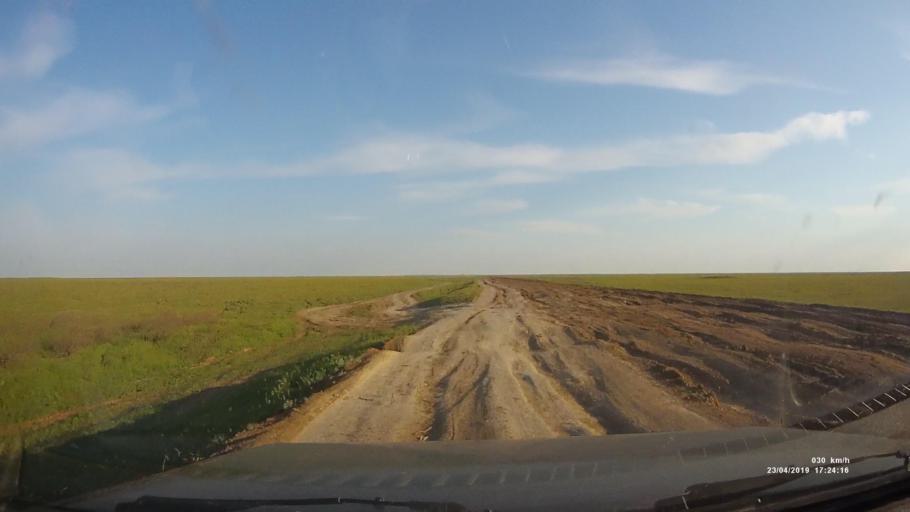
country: RU
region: Kalmykiya
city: Priyutnoye
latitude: 46.1577
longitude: 43.5085
